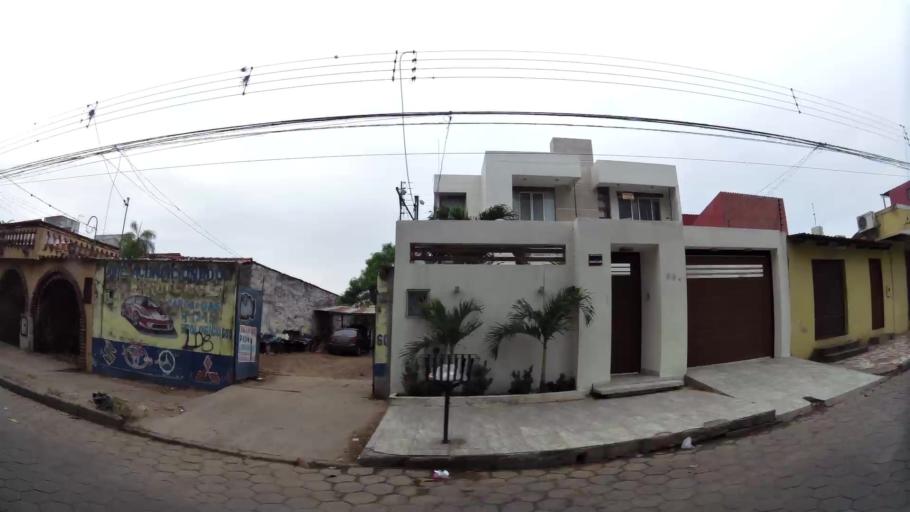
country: BO
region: Santa Cruz
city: Santa Cruz de la Sierra
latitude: -17.7981
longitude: -63.1874
